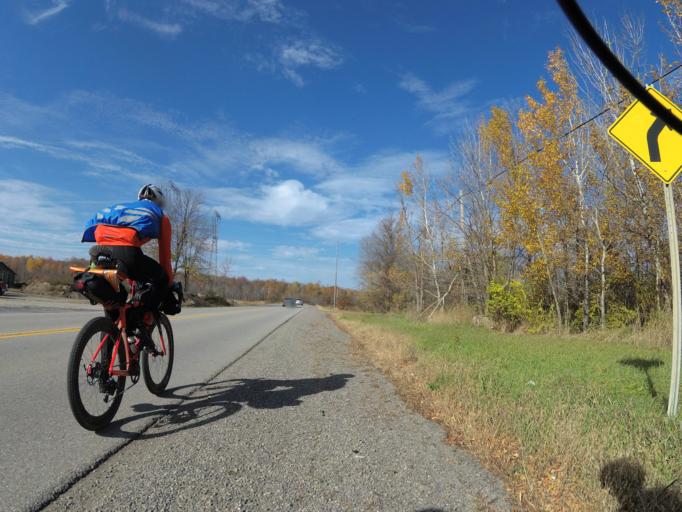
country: CA
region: Ontario
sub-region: Lanark County
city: Smiths Falls
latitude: 44.8935
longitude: -76.0122
